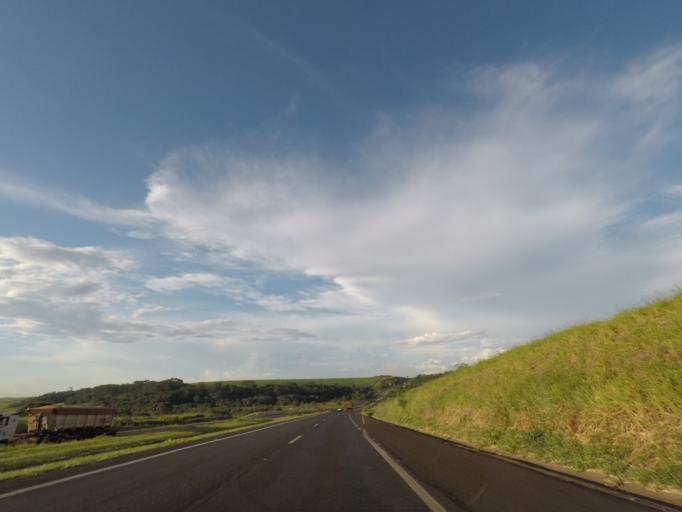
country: BR
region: Sao Paulo
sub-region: Ituverava
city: Ituverava
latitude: -20.2623
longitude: -47.7996
